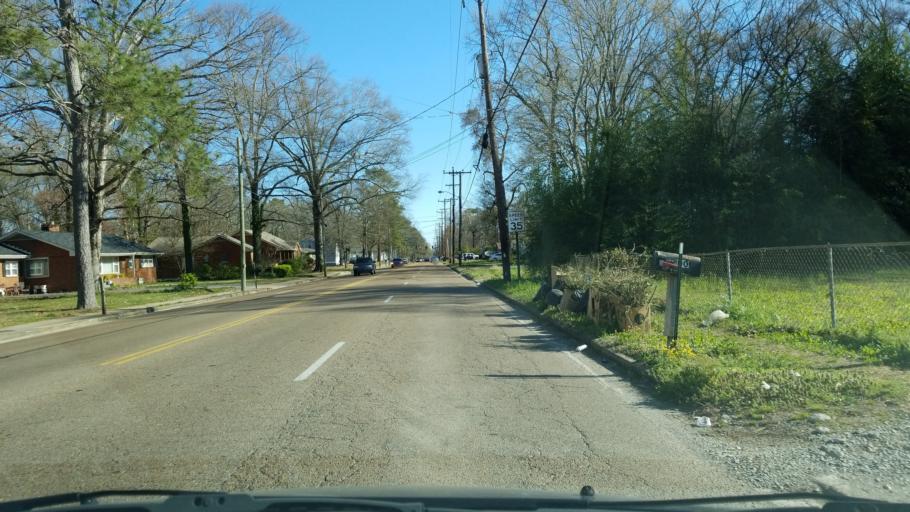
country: US
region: Tennessee
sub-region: Hamilton County
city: East Ridge
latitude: 35.0145
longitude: -85.2274
